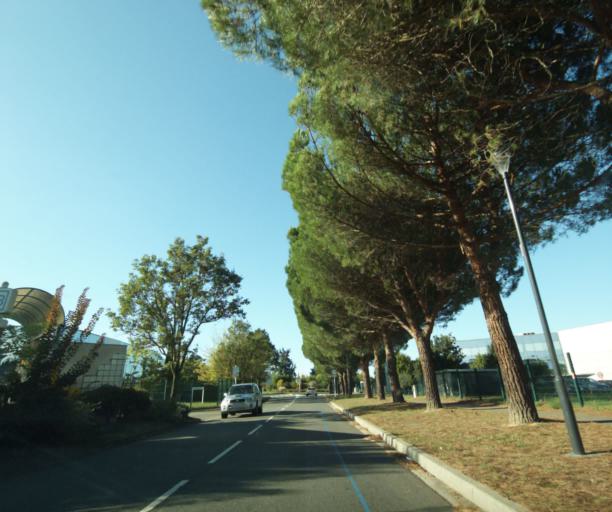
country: FR
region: Midi-Pyrenees
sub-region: Departement de la Haute-Garonne
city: Balma
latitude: 43.5805
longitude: 1.4950
